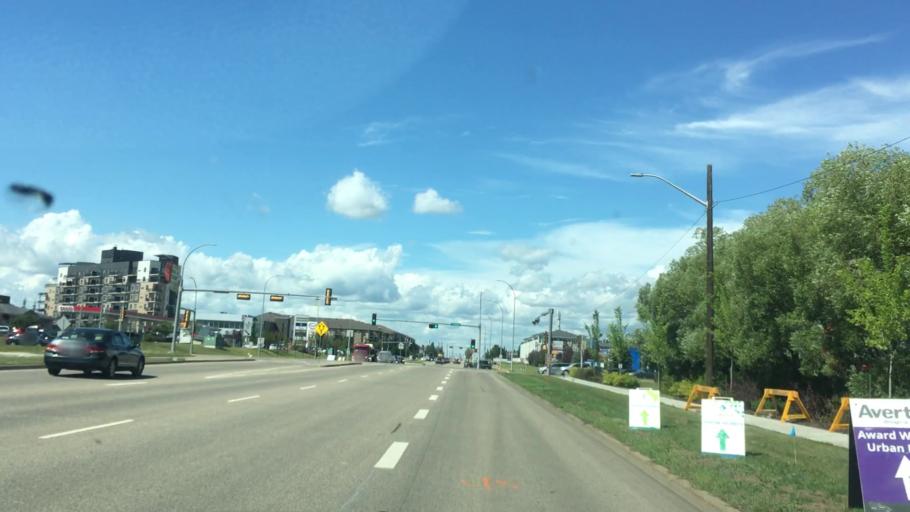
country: CA
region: Alberta
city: Beaumont
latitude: 53.4250
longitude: -113.5150
